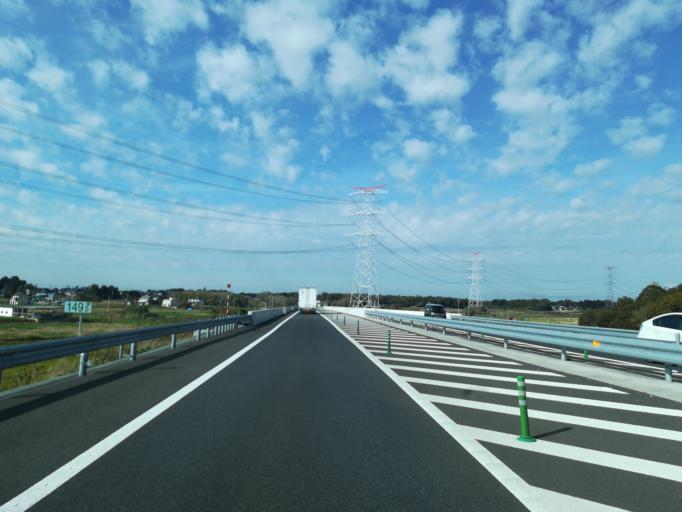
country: JP
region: Ibaraki
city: Mitsukaido
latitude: 36.0597
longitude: 140.0417
